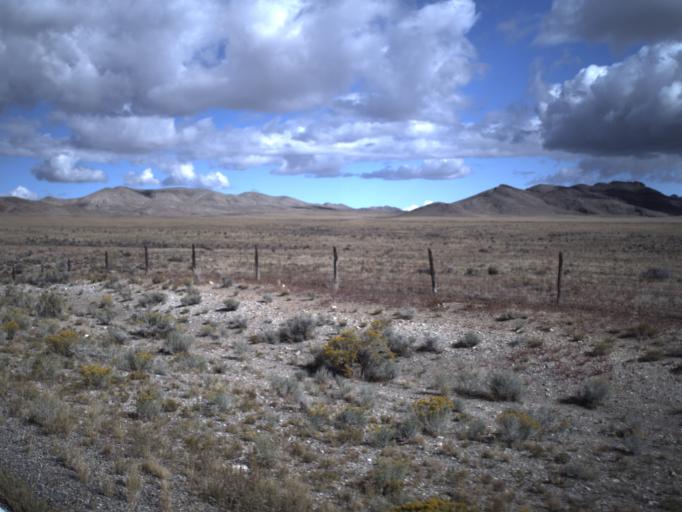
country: US
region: Utah
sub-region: Beaver County
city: Milford
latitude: 38.5907
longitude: -113.8197
